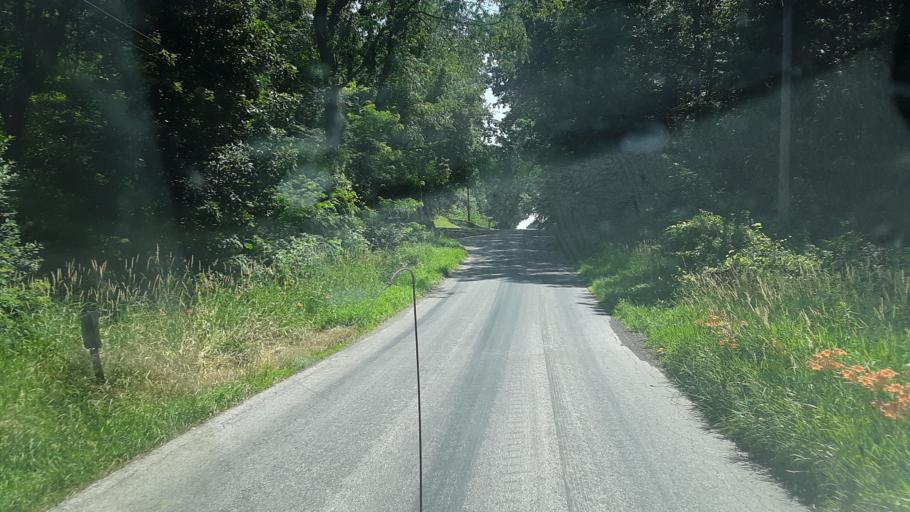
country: US
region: Ohio
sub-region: Wayne County
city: Shreve
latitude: 40.7196
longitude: -82.0343
